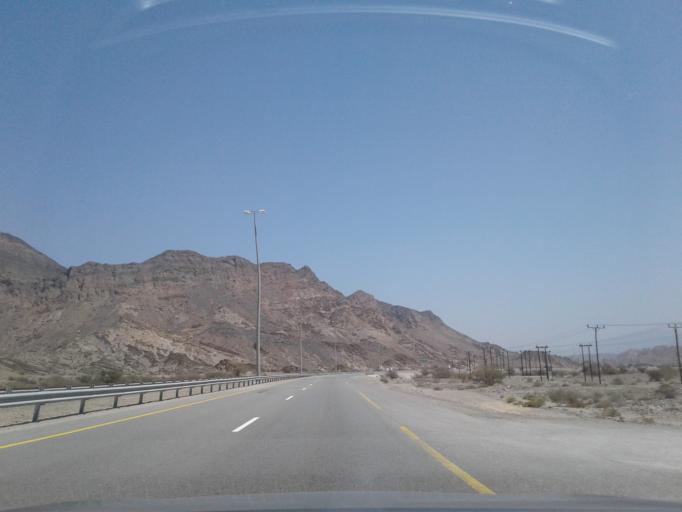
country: OM
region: Muhafazat Masqat
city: Muscat
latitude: 23.3014
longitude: 58.7372
